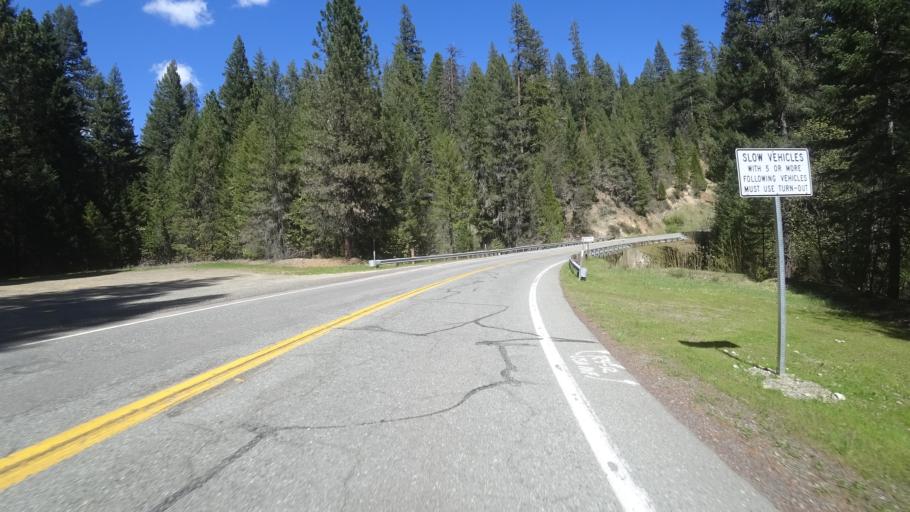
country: US
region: California
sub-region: Trinity County
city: Lewiston
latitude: 40.8687
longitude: -122.8122
